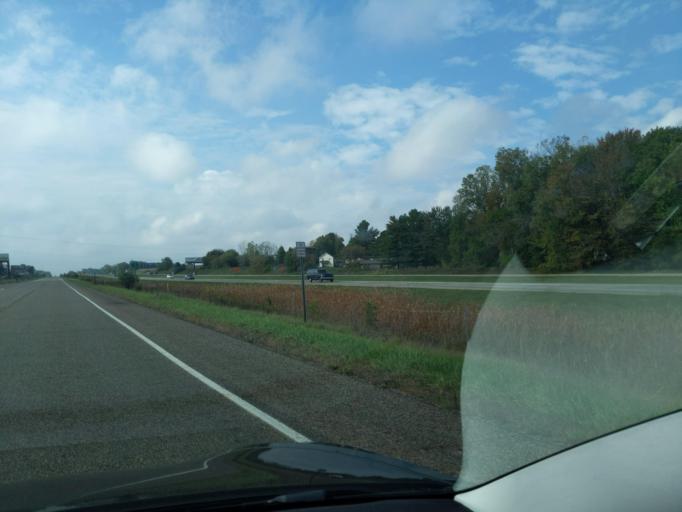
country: US
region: Michigan
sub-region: Eaton County
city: Potterville
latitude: 42.5978
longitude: -84.7819
